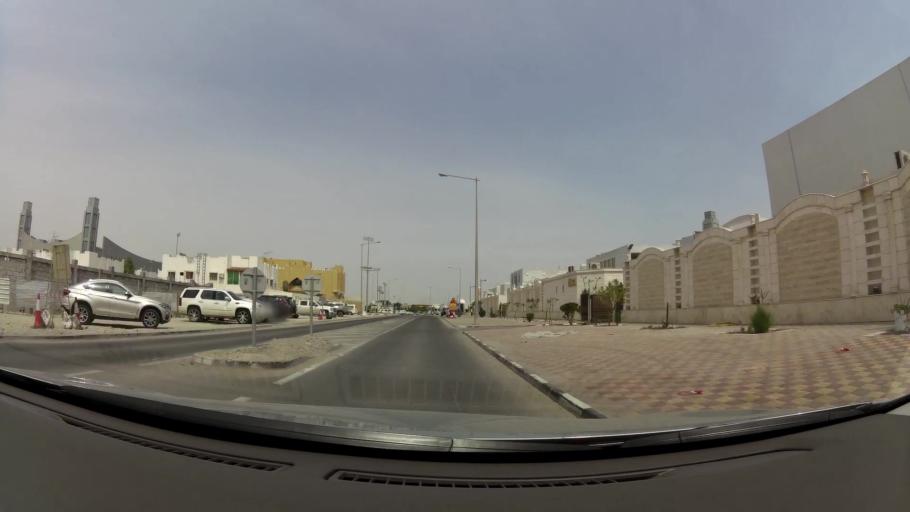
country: QA
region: Baladiyat ad Dawhah
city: Doha
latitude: 25.2648
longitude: 51.4834
